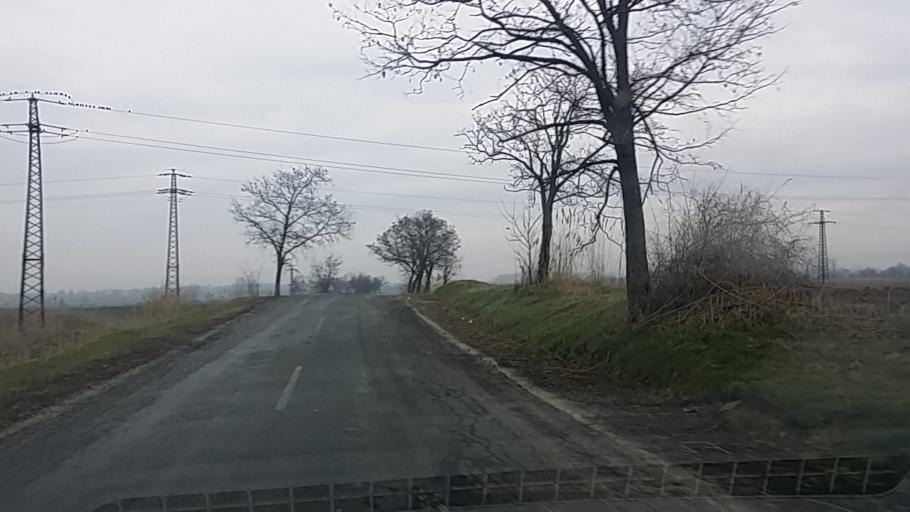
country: HU
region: Komarom-Esztergom
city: Tat
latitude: 47.7343
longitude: 18.6214
